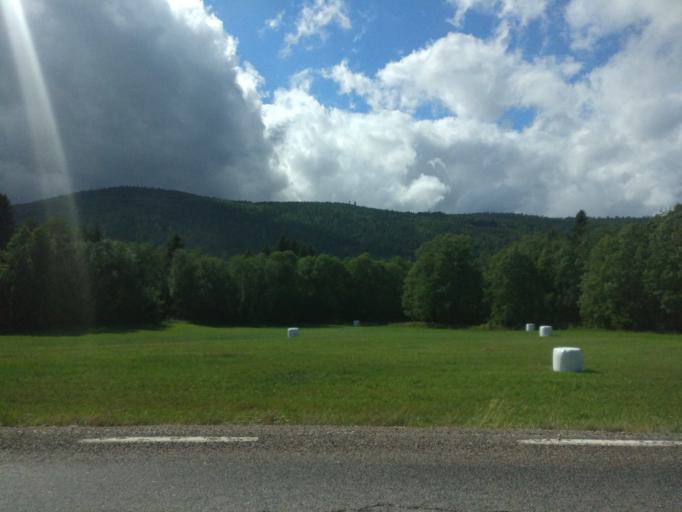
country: SE
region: Vaermland
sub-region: Hagfors Kommun
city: Ekshaerad
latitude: 60.3637
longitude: 13.3104
